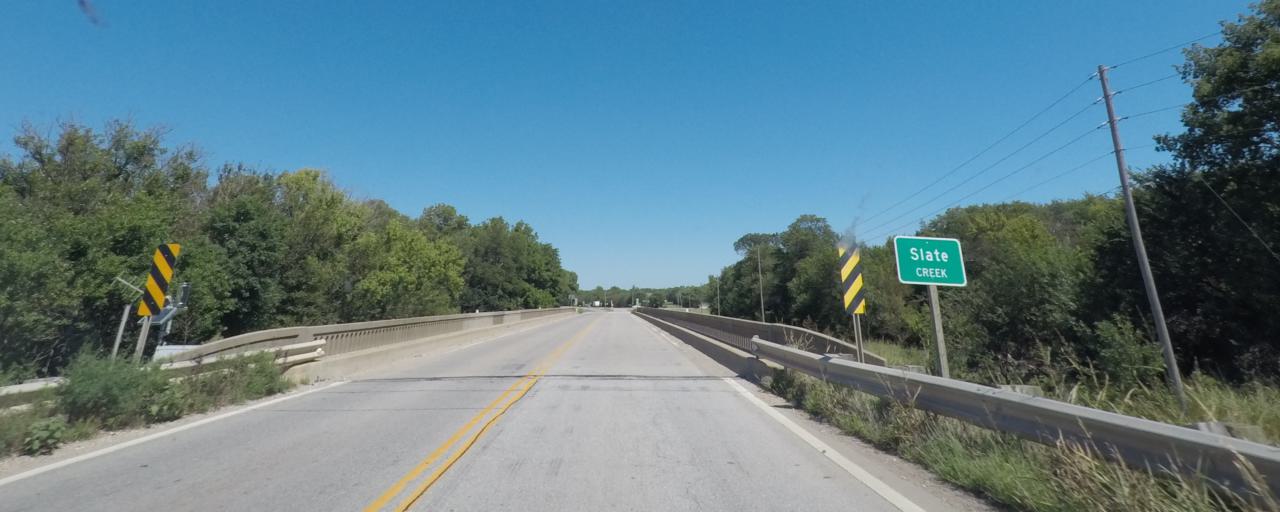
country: US
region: Kansas
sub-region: Sumner County
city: Wellington
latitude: 37.2495
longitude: -97.4035
